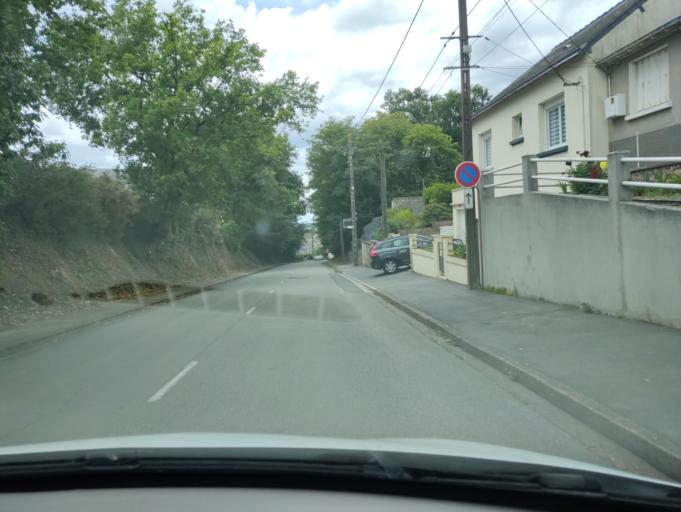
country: FR
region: Pays de la Loire
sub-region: Departement de la Loire-Atlantique
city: Chateaubriant
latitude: 47.7165
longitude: -1.3665
